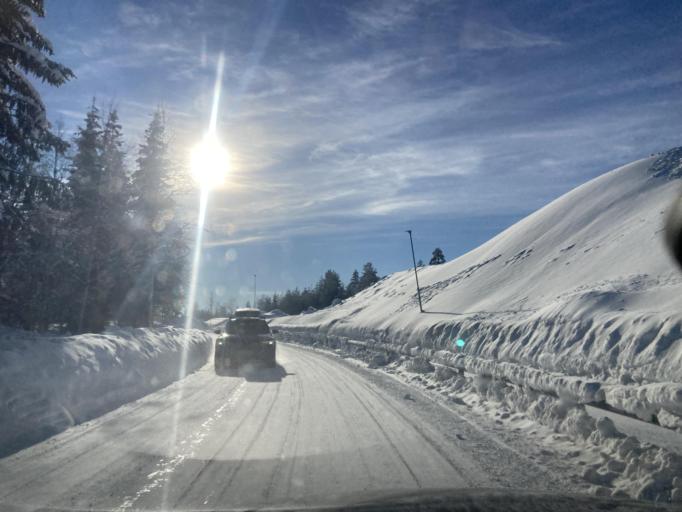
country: NO
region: Hedmark
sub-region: Trysil
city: Innbygda
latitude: 61.3023
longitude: 12.2444
